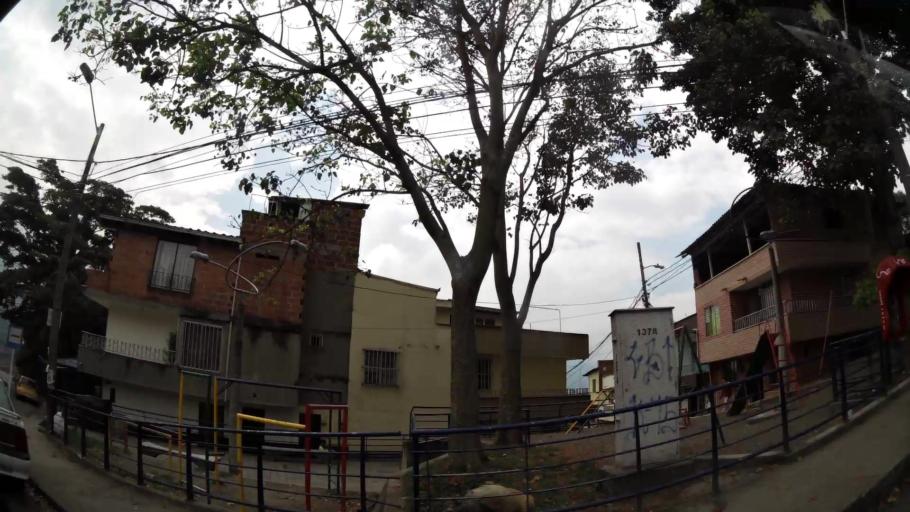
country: CO
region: Antioquia
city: Itagui
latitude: 6.1997
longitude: -75.5930
